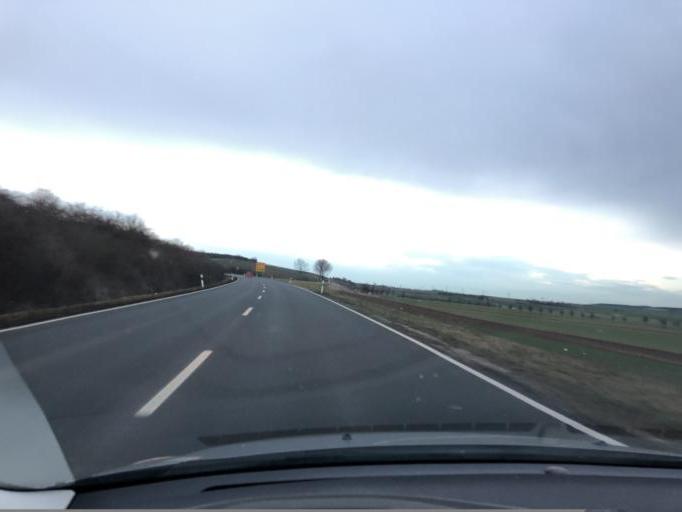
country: DE
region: Saxony-Anhalt
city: Freyburg
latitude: 51.2004
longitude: 11.7871
